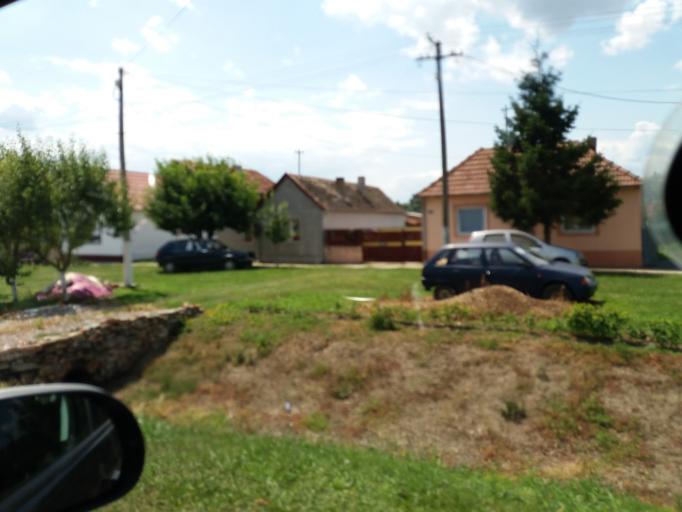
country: RS
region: Autonomna Pokrajina Vojvodina
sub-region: Sremski Okrug
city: Pecinci
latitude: 44.8510
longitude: 19.9614
